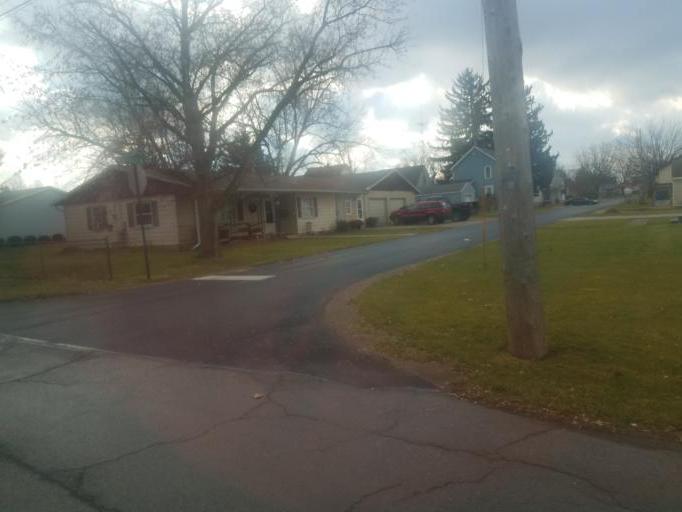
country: US
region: Ohio
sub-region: Marion County
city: Marion
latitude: 40.5763
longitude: -83.1517
